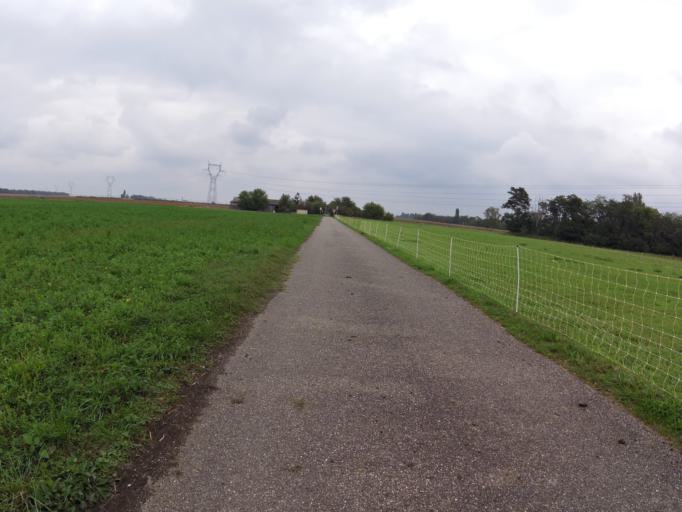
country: FR
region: Alsace
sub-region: Departement du Haut-Rhin
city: Fessenheim
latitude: 47.9373
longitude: 7.5392
